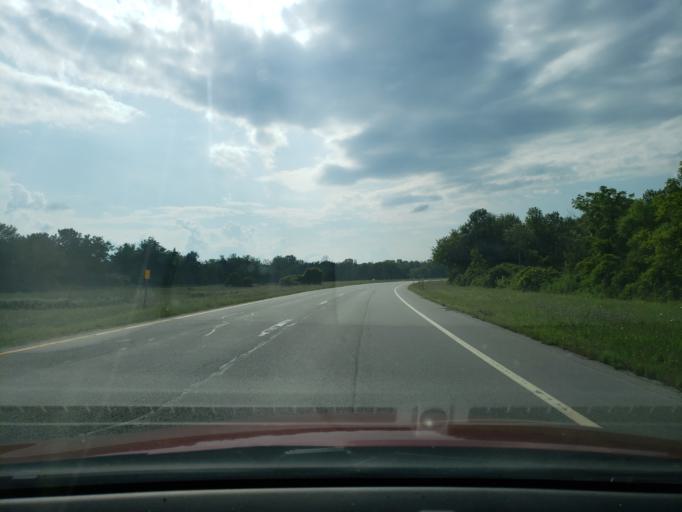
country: US
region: New York
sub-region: Monroe County
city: Greece
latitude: 43.2720
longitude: -77.6821
